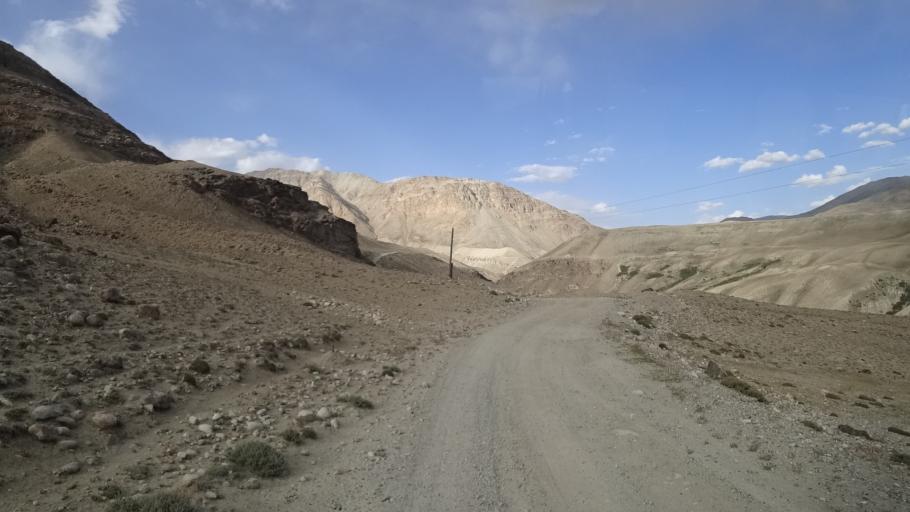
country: AF
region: Badakhshan
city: Khandud
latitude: 37.2246
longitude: 72.8006
